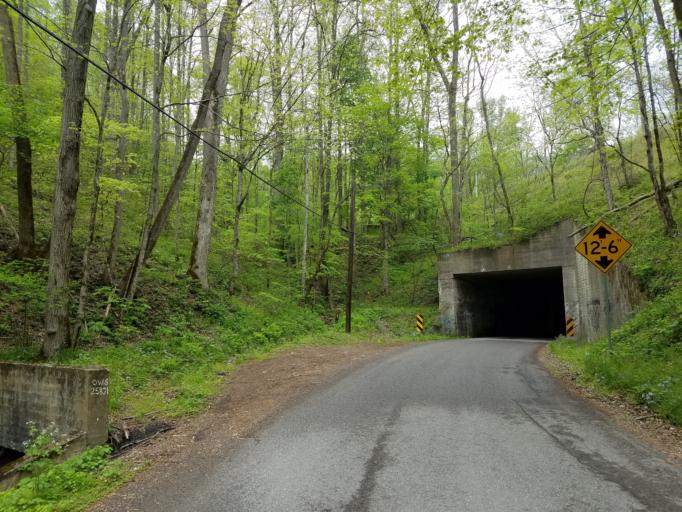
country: US
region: Kentucky
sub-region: Harlan County
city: Harlan
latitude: 36.7016
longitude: -83.2892
